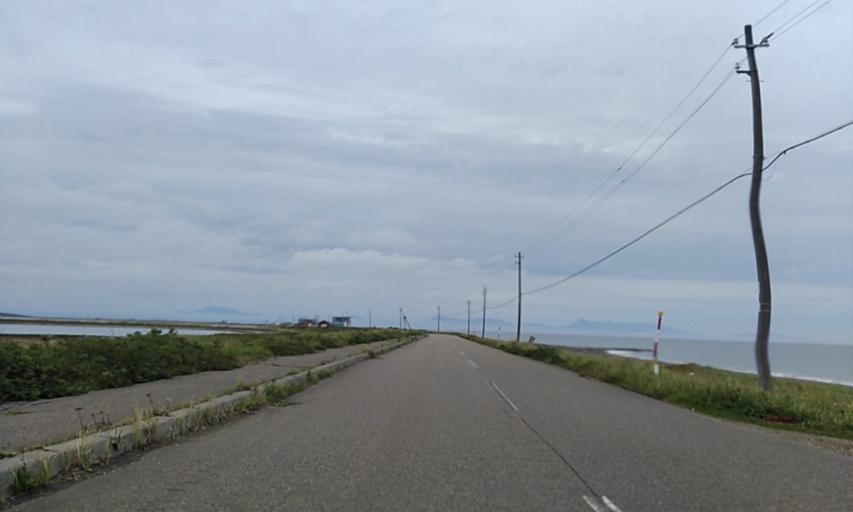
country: JP
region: Hokkaido
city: Shibetsu
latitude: 43.5855
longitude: 145.3407
